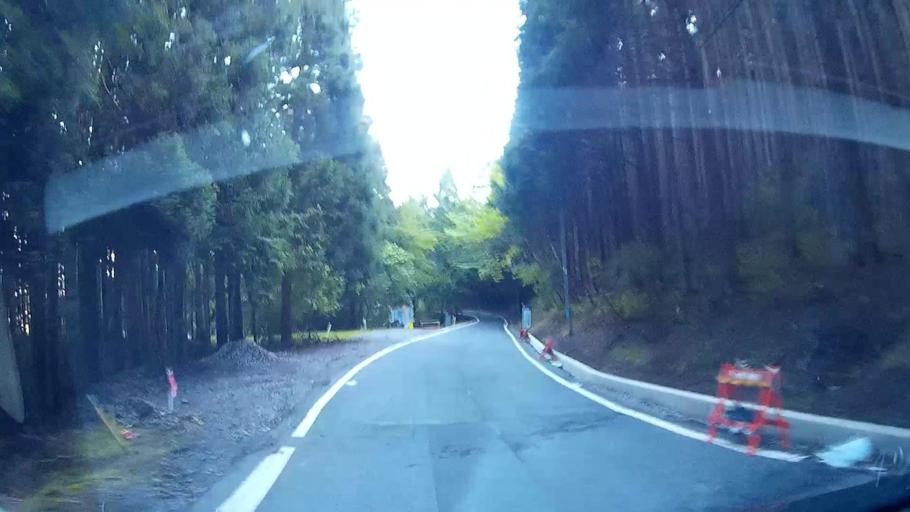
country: JP
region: Shizuoka
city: Shizuoka-shi
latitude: 35.1834
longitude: 138.2493
